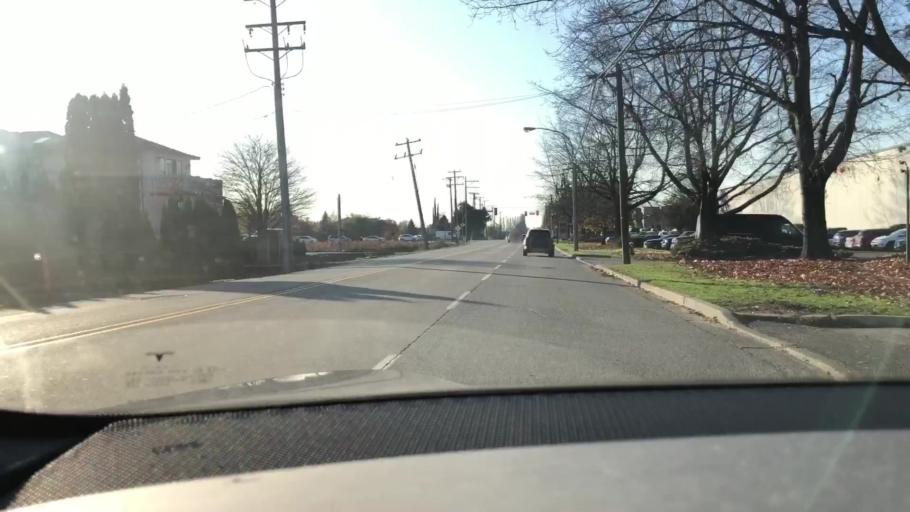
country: CA
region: British Columbia
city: Richmond
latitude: 49.1858
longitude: -123.0691
